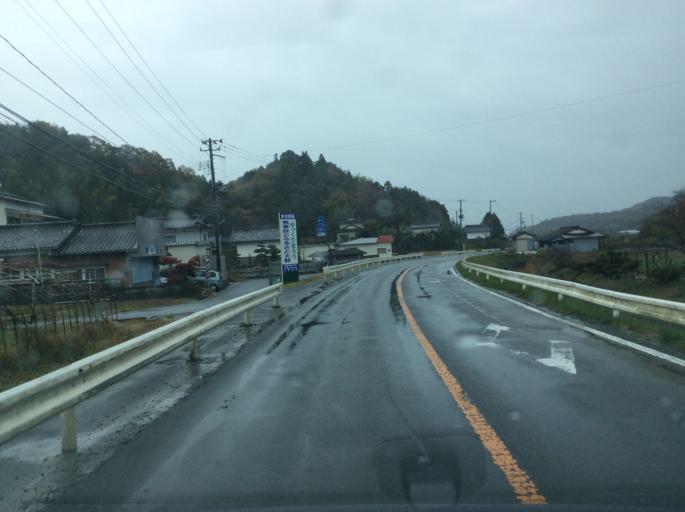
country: JP
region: Fukushima
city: Iwaki
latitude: 37.1144
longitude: 140.9305
